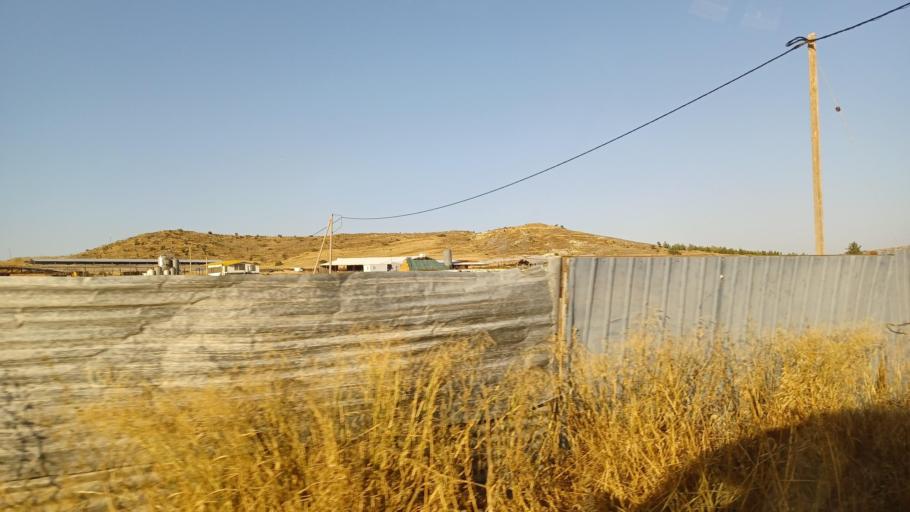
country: CY
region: Larnaka
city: Athienou
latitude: 35.0501
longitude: 33.5093
